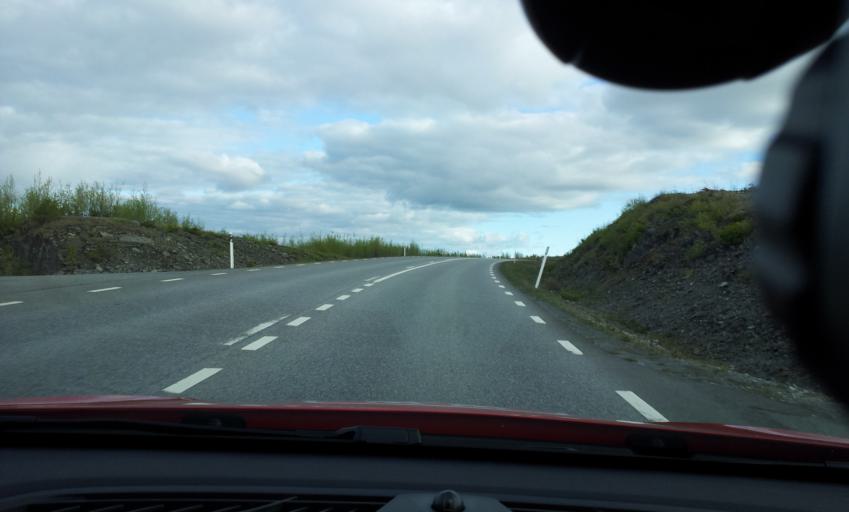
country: SE
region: Jaemtland
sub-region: OEstersunds Kommun
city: Ostersund
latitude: 63.1876
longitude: 14.5348
